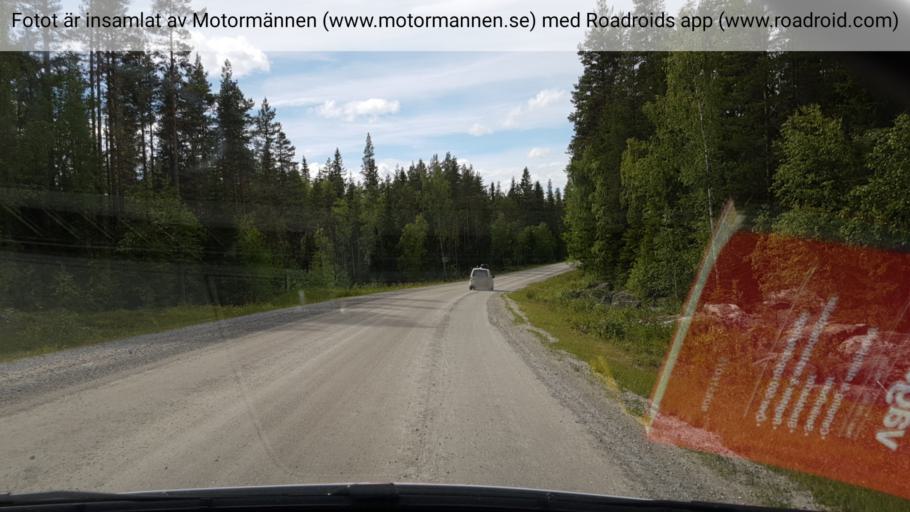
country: SE
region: Vaesternorrland
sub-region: Solleftea Kommun
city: Solleftea
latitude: 63.3119
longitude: 17.2703
